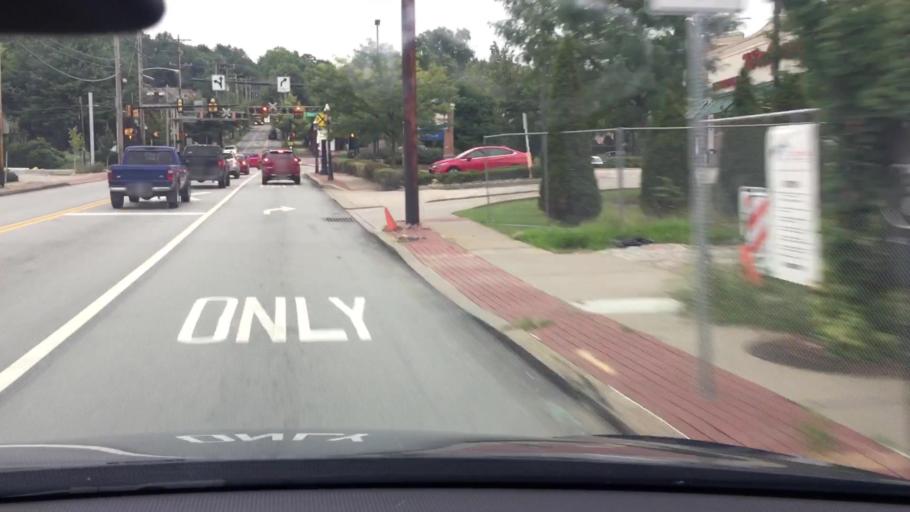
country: US
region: Pennsylvania
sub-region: Allegheny County
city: Oakmont
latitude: 40.5259
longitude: -79.8422
